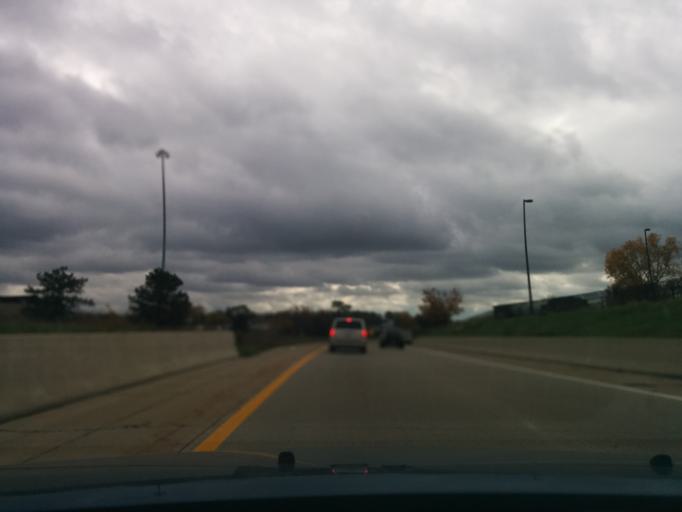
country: US
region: Michigan
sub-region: Oakland County
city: Southfield
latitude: 42.4565
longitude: -83.2210
